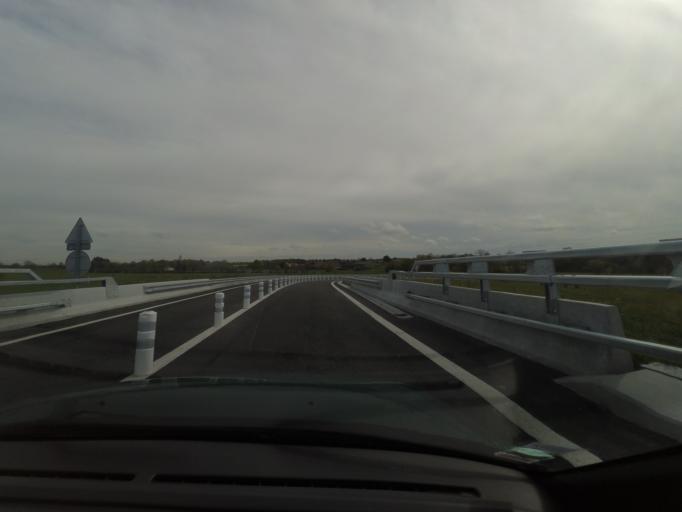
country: FR
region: Pays de la Loire
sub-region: Departement de la Loire-Atlantique
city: Aigrefeuille-sur-Maine
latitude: 47.0725
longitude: -1.4373
